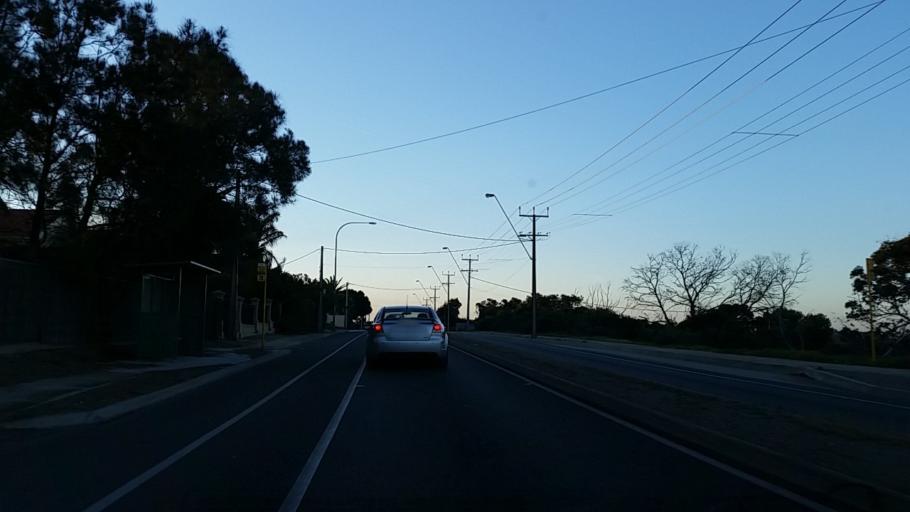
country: AU
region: South Australia
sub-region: Adelaide
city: Port Noarlunga
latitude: -35.1591
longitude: 138.4750
